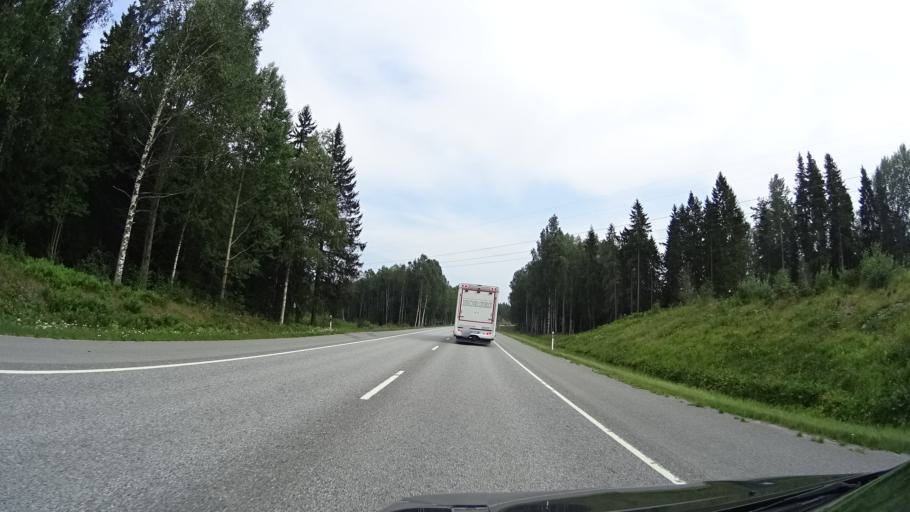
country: FI
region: Uusimaa
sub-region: Raaseporin
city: Karis
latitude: 60.0752
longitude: 23.7646
